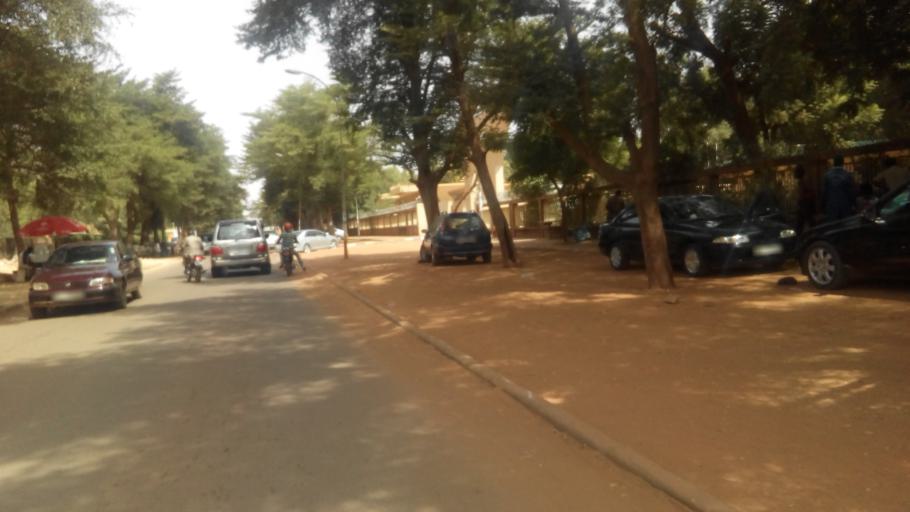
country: NE
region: Niamey
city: Niamey
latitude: 13.5211
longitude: 2.1046
